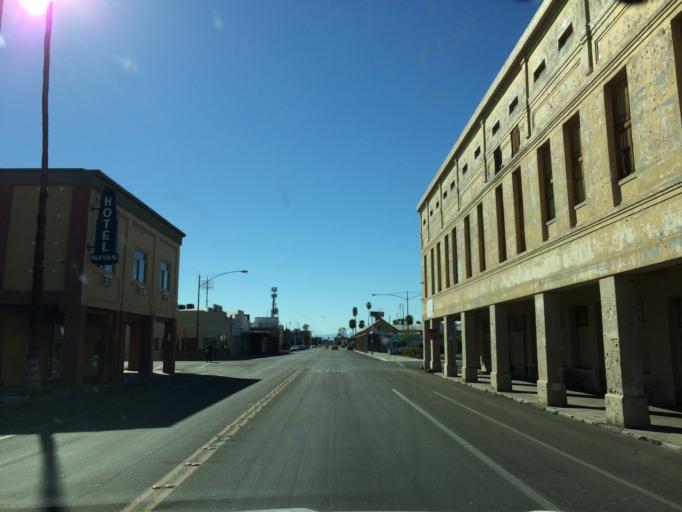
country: US
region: California
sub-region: Imperial County
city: El Centro
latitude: 32.7918
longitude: -115.5563
